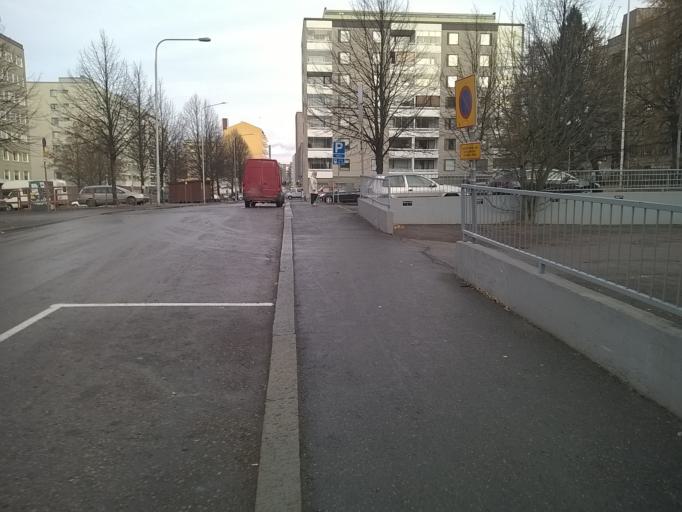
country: FI
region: Pirkanmaa
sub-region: Tampere
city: Tampere
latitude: 61.4995
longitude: 23.7778
